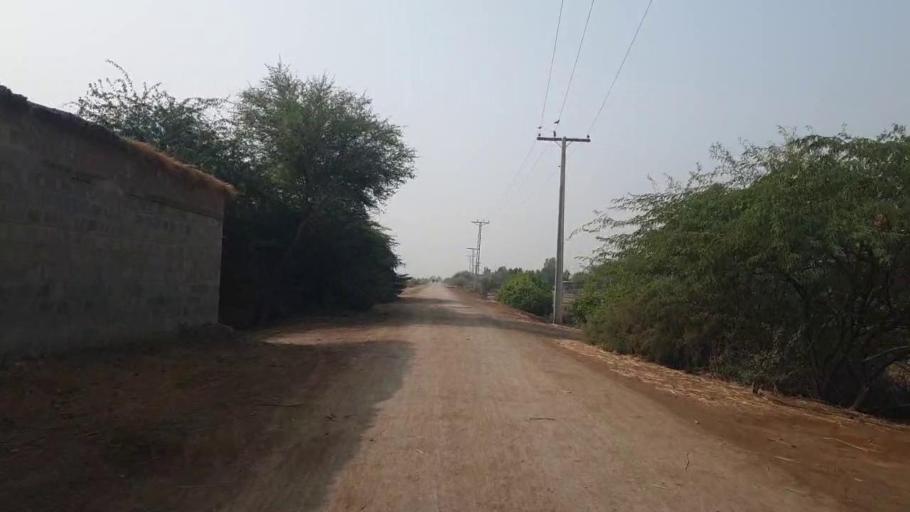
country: PK
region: Sindh
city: Tando Muhammad Khan
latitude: 25.2738
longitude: 68.4878
